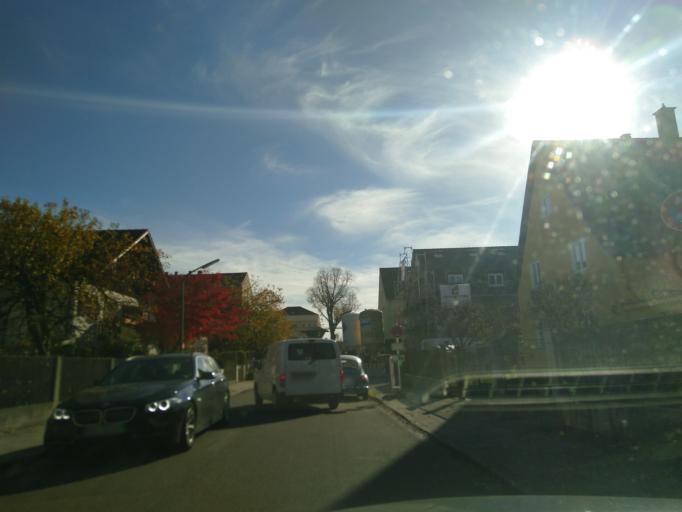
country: DE
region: Bavaria
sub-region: Upper Bavaria
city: Munich
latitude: 48.1016
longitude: 11.5885
